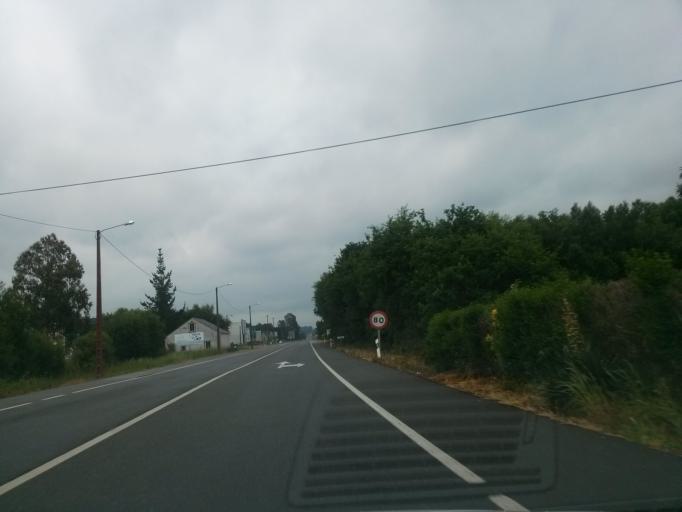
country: ES
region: Galicia
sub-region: Provincia de Lugo
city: Begonte
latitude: 43.1600
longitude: -7.6979
